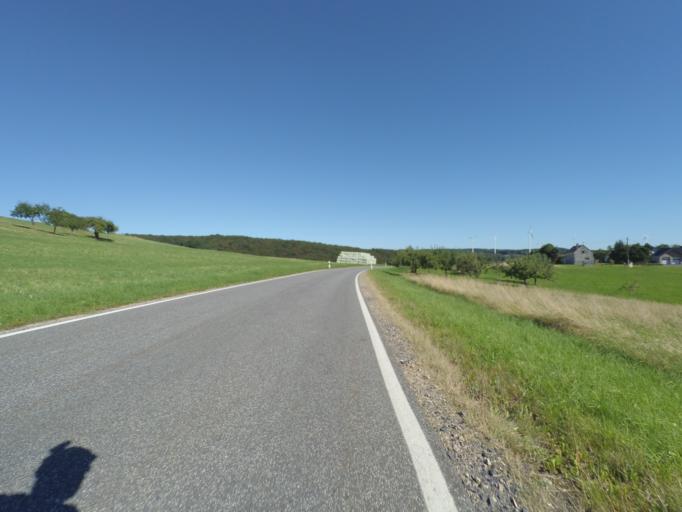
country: DE
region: Rheinland-Pfalz
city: Boxberg
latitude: 50.2728
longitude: 6.8783
